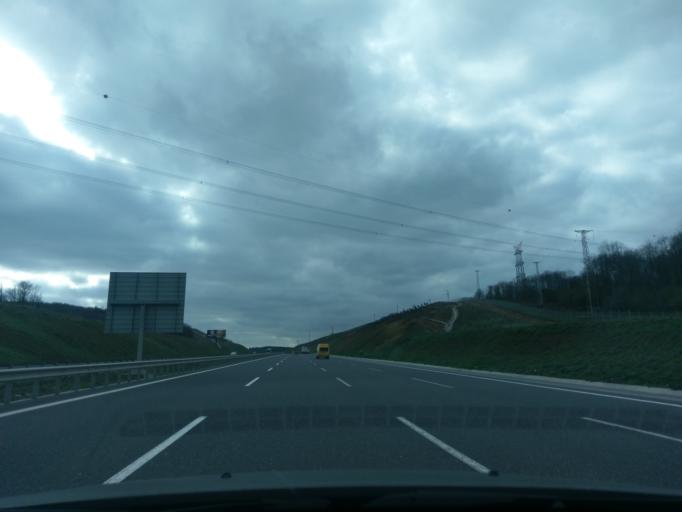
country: TR
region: Istanbul
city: Basaksehir
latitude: 41.1802
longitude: 28.8153
